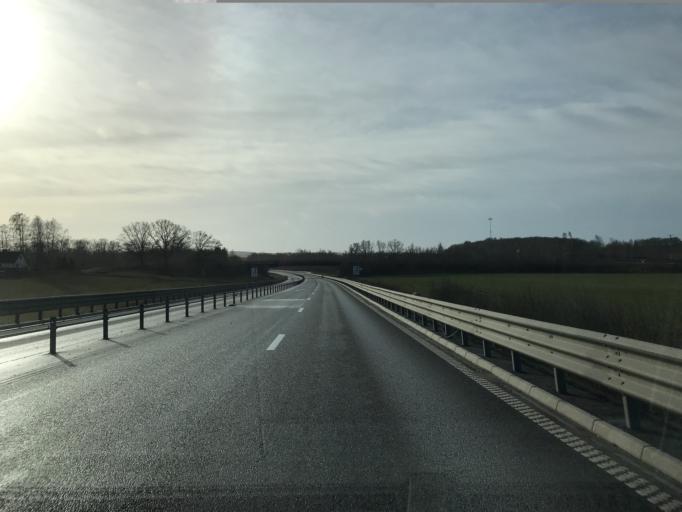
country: SE
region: Skane
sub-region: Hassleholms Kommun
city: Hassleholm
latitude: 56.1473
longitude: 13.8202
